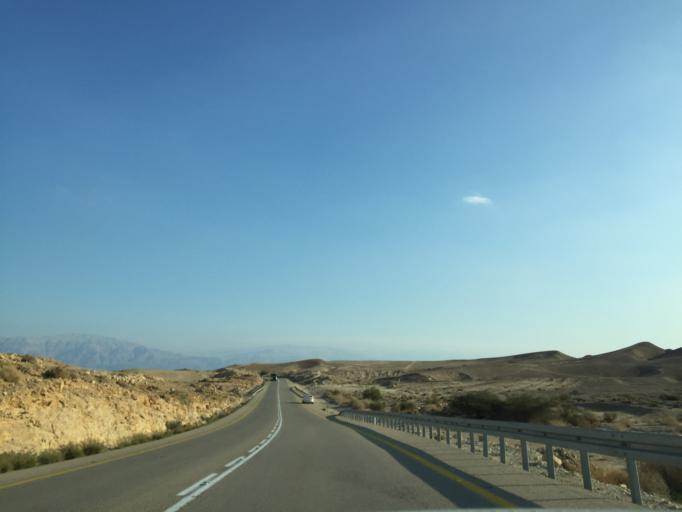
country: IL
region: Southern District
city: `En Boqeq
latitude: 31.1655
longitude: 35.3206
